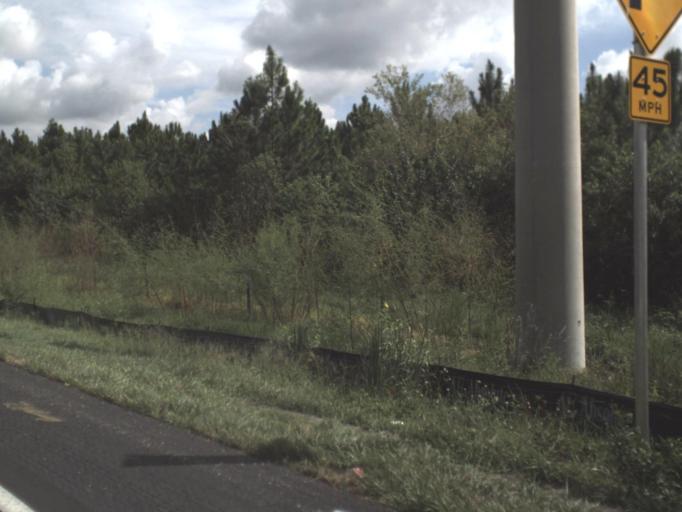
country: US
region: Florida
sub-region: Polk County
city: Combee Settlement
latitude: 28.0788
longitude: -81.9081
